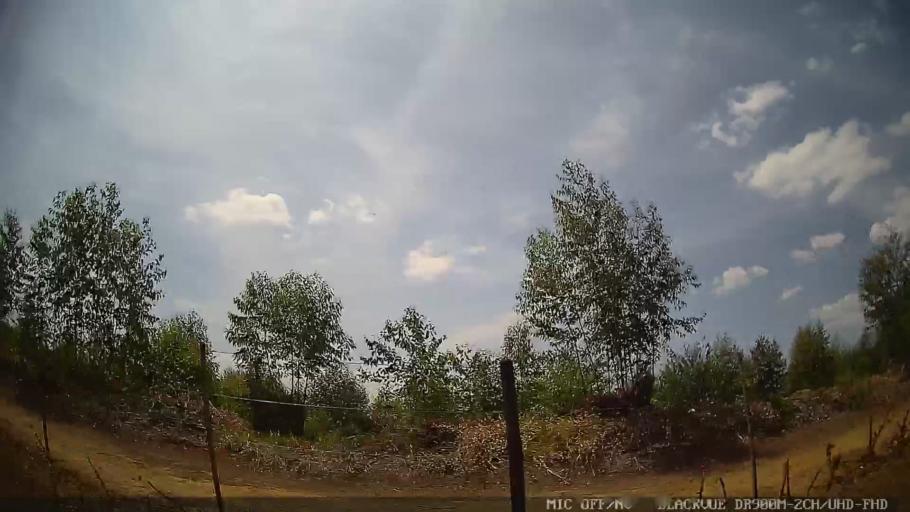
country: BR
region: Sao Paulo
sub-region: Itupeva
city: Itupeva
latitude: -23.2515
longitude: -47.0454
